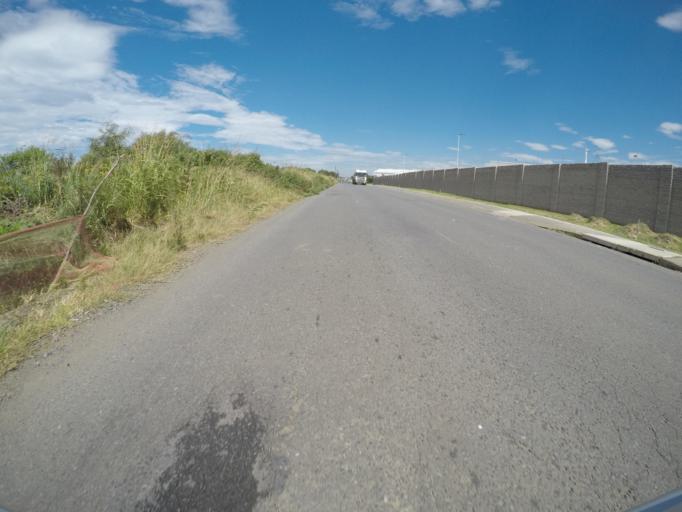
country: ZA
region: Eastern Cape
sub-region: Buffalo City Metropolitan Municipality
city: East London
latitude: -33.0336
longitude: 27.8908
